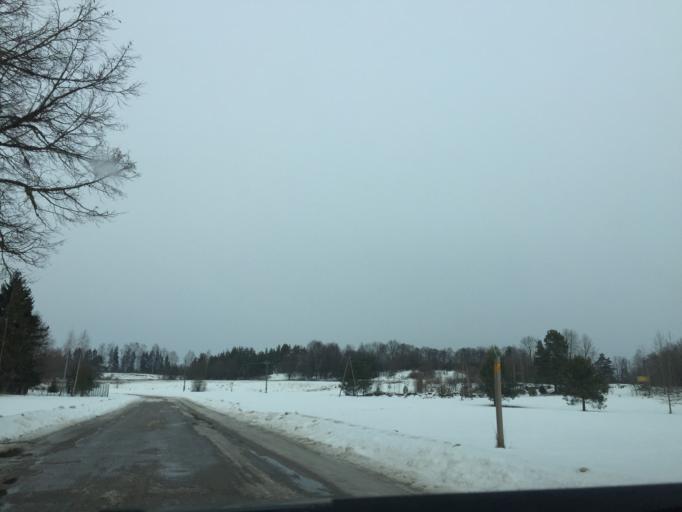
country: LV
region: Ikskile
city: Ikskile
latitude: 56.8428
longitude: 24.4719
